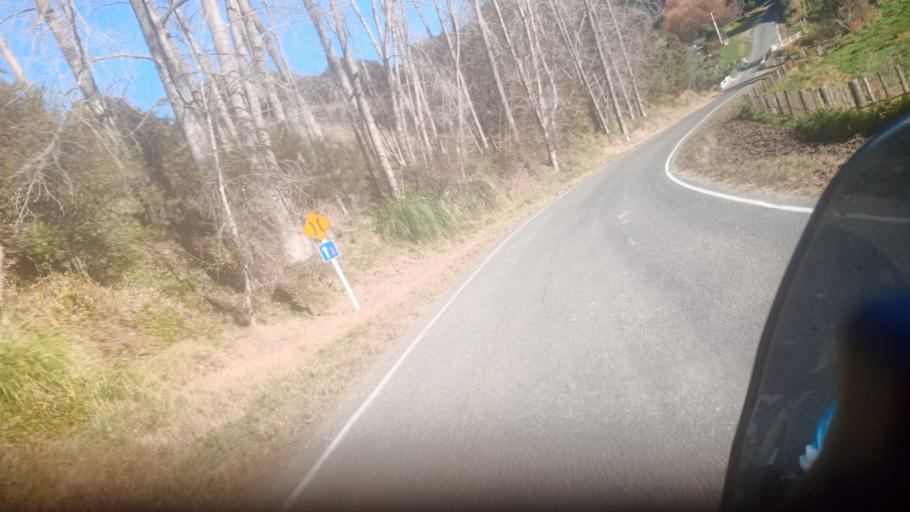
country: NZ
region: Gisborne
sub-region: Gisborne District
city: Gisborne
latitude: -38.5604
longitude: 177.6226
